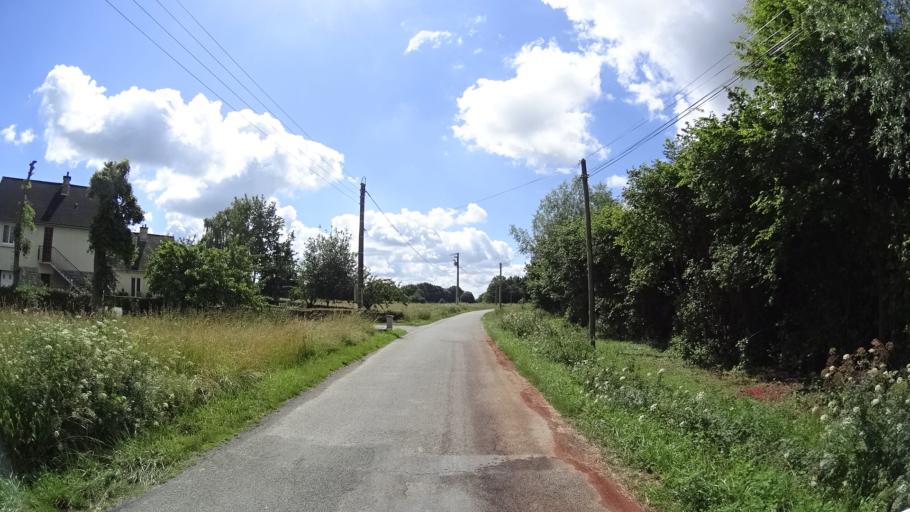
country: FR
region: Brittany
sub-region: Departement d'Ille-et-Vilaine
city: Le Rheu
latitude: 48.1153
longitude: -1.8158
